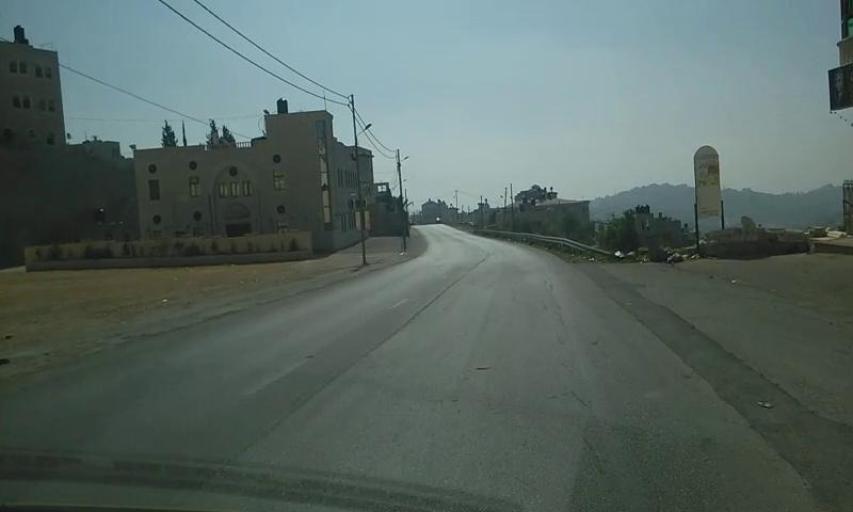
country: PS
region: West Bank
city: Dayr Jarir
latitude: 31.9675
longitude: 35.2908
